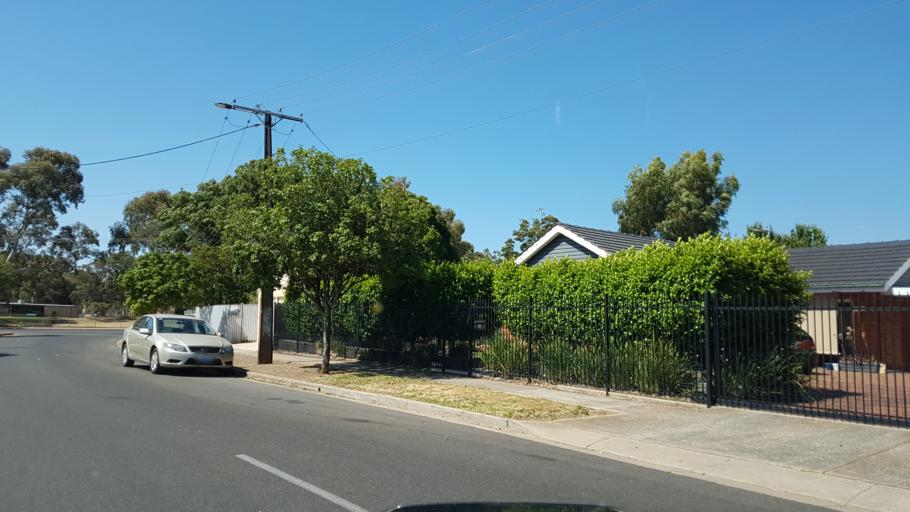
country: AU
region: South Australia
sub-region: Marion
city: Clovelly Park
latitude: -35.0043
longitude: 138.5646
